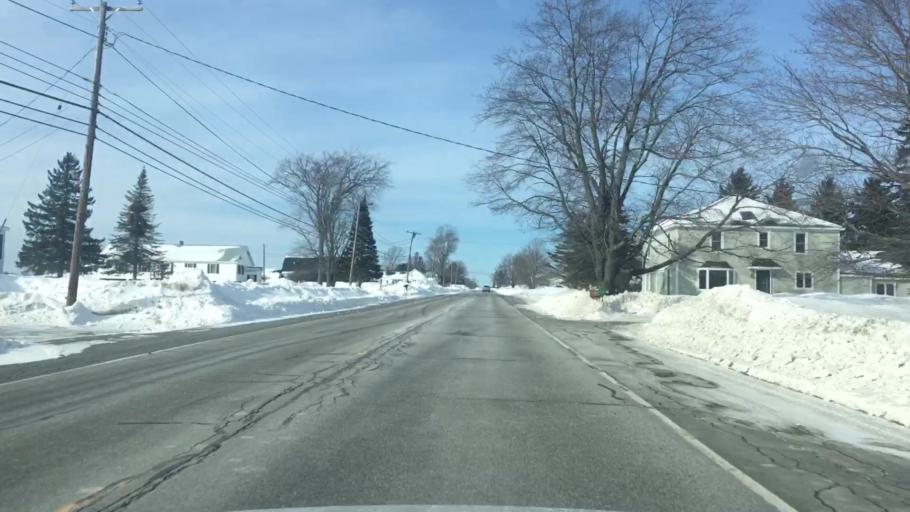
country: US
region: Maine
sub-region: Penobscot County
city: Charleston
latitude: 45.0228
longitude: -69.0295
